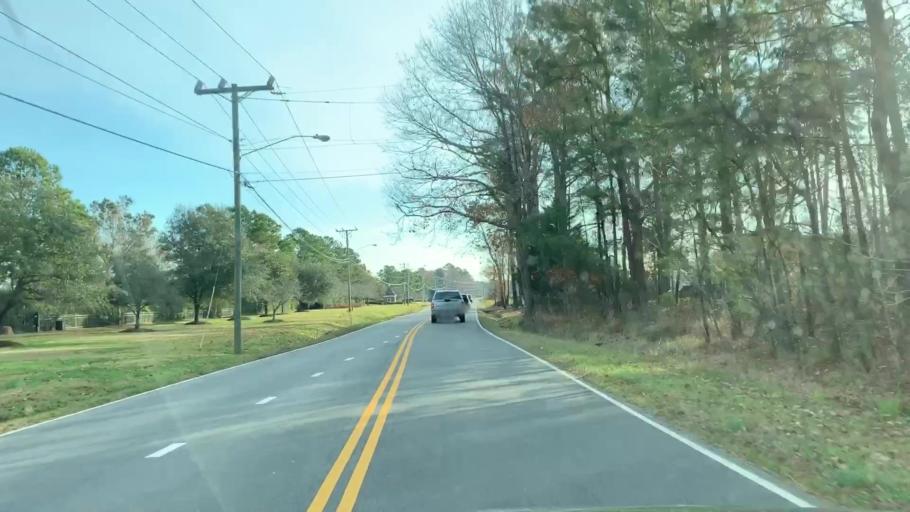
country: US
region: Virginia
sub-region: City of Virginia Beach
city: Virginia Beach
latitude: 36.7231
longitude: -76.0618
